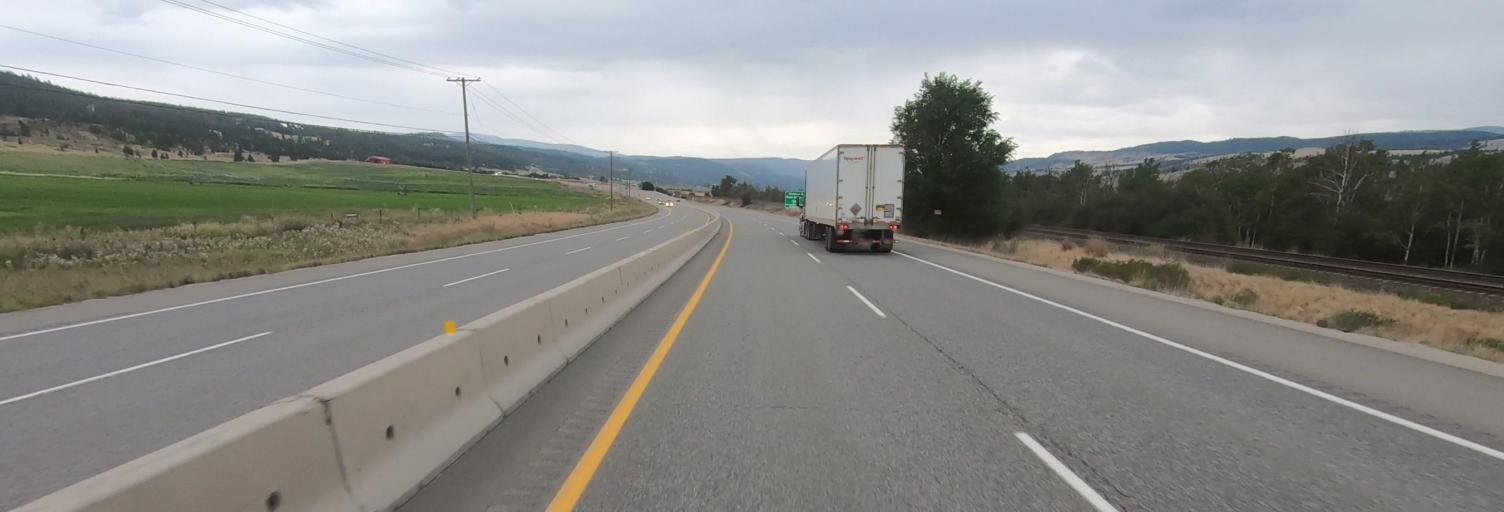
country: CA
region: British Columbia
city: Chase
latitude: 50.6959
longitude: -119.8067
